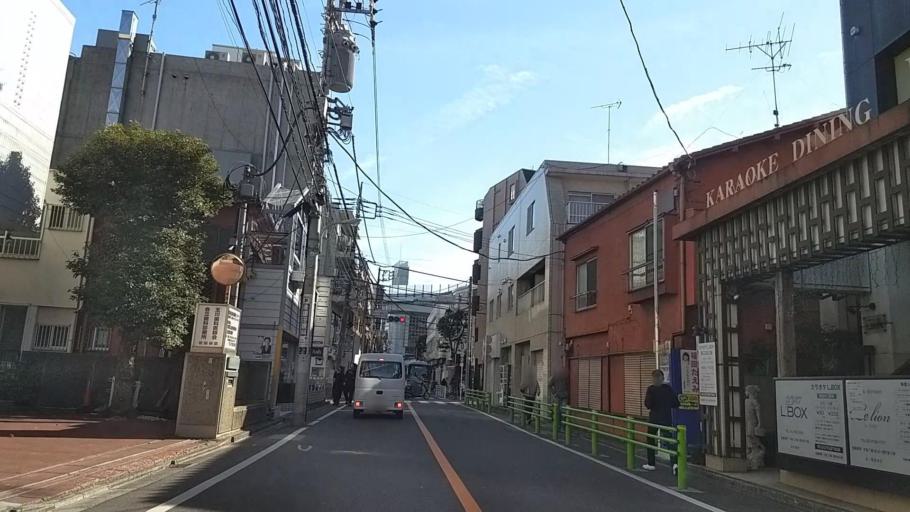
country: JP
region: Tokyo
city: Chofugaoka
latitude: 35.6157
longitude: 139.6250
